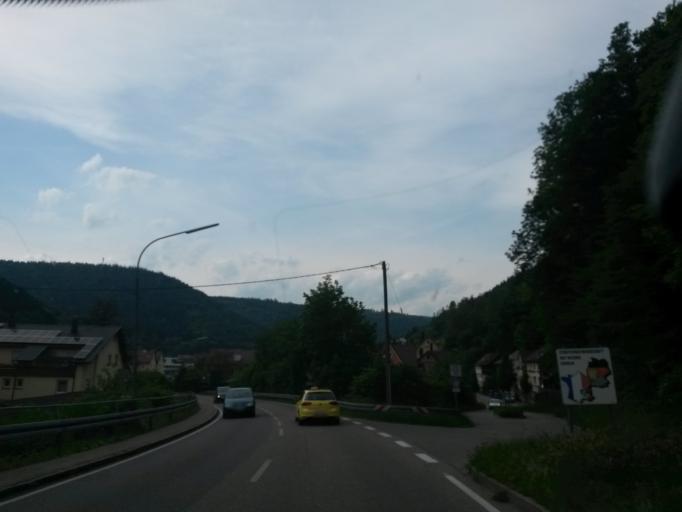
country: DE
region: Baden-Wuerttemberg
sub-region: Karlsruhe Region
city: Hofen an der Enz
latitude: 48.7695
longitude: 8.5860
